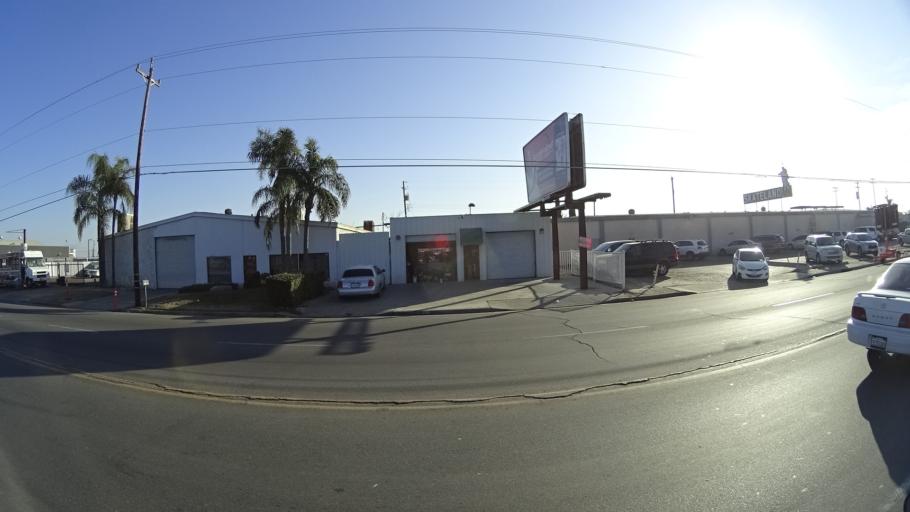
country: US
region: California
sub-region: Kern County
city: Bakersfield
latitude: 35.3394
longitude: -119.0067
